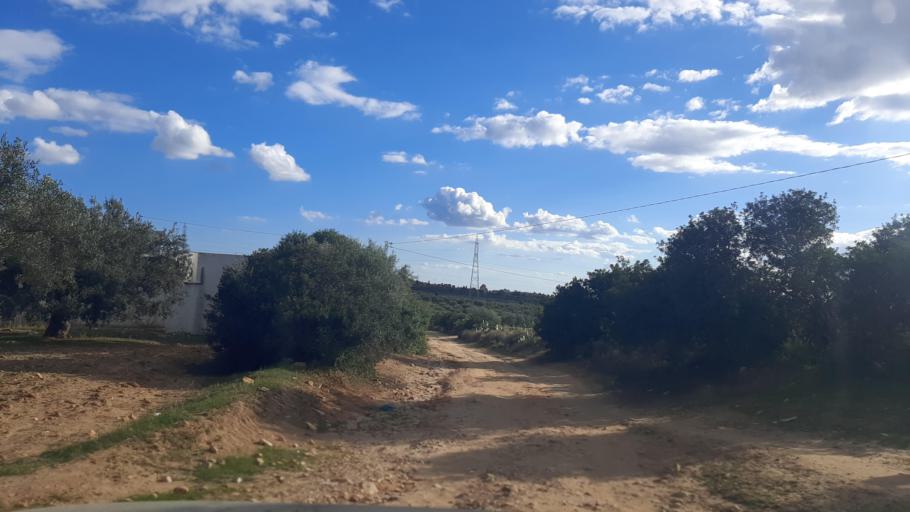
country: TN
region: Nabul
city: Bu `Urqub
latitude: 36.4423
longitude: 10.5068
